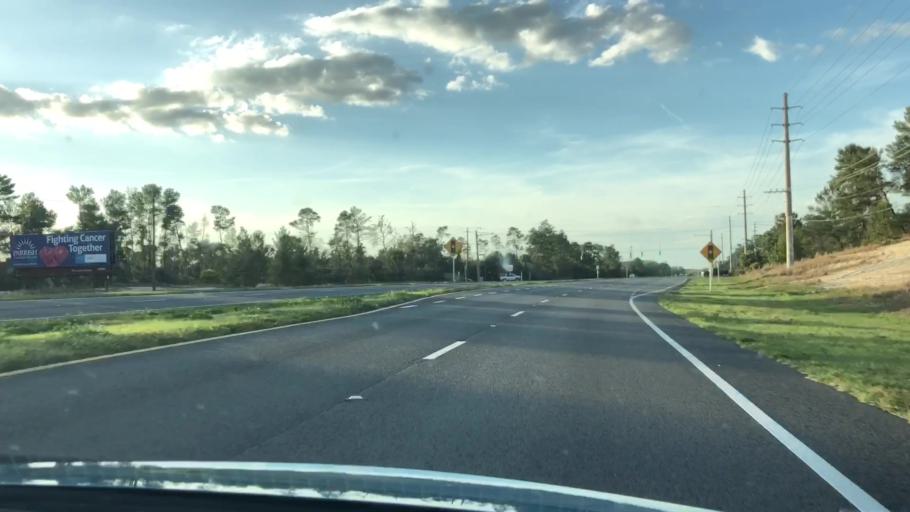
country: US
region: Florida
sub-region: Brevard County
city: Port Saint John
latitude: 28.5355
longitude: -80.8252
